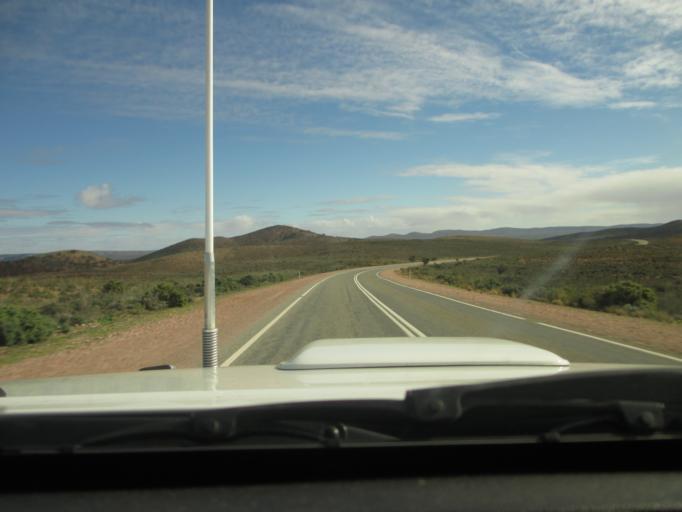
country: AU
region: South Australia
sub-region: Flinders Ranges
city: Quorn
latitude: -31.8077
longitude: 138.3639
